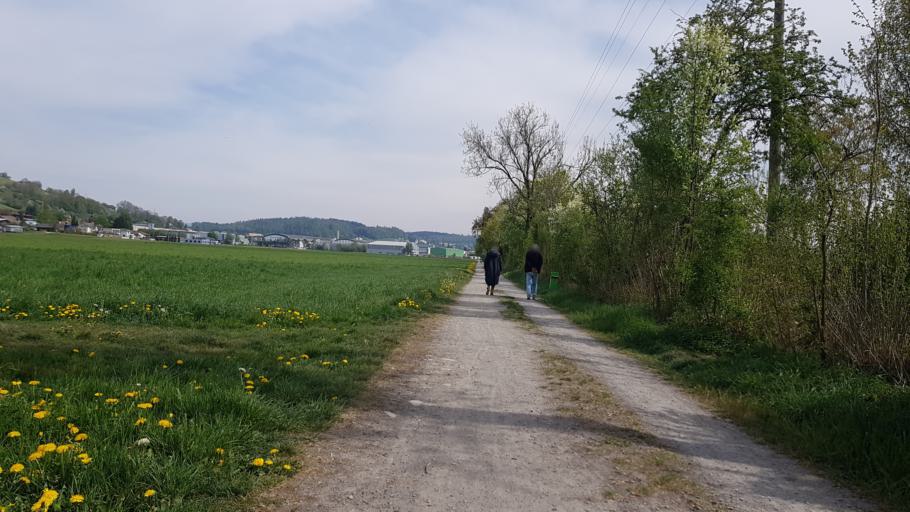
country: CH
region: Aargau
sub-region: Bezirk Kulm
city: Gontenschwil
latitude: 47.2725
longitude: 8.1599
